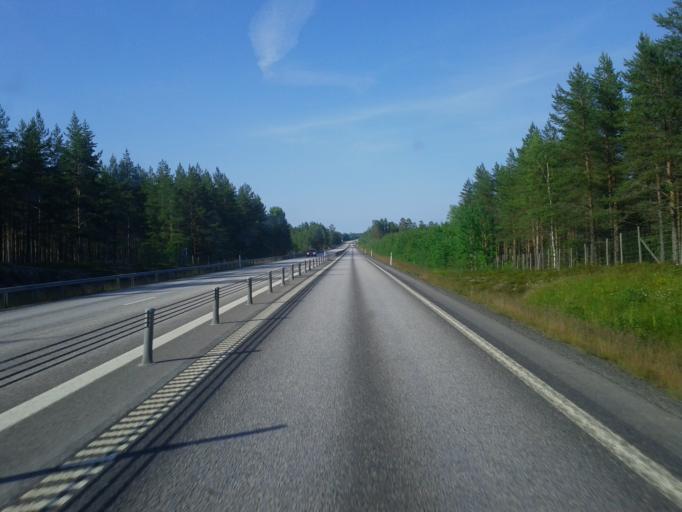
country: SE
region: Vaesterbotten
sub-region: Umea Kommun
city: Saevar
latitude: 63.9406
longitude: 20.6513
